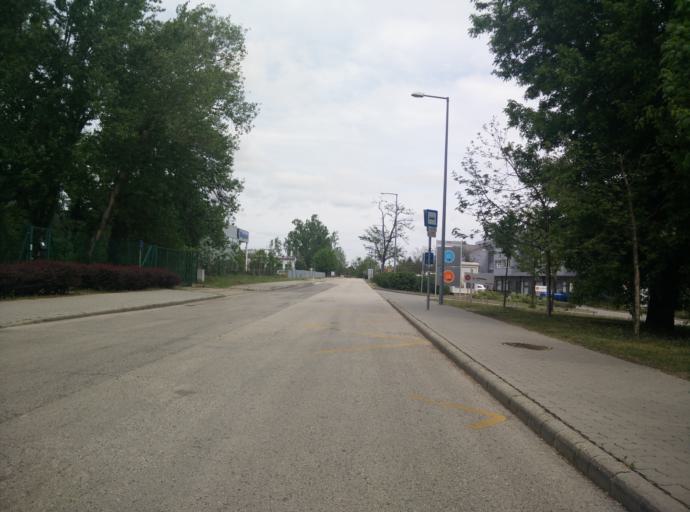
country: HU
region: Budapest
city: Budapest XV. keruelet
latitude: 47.6050
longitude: 19.1036
